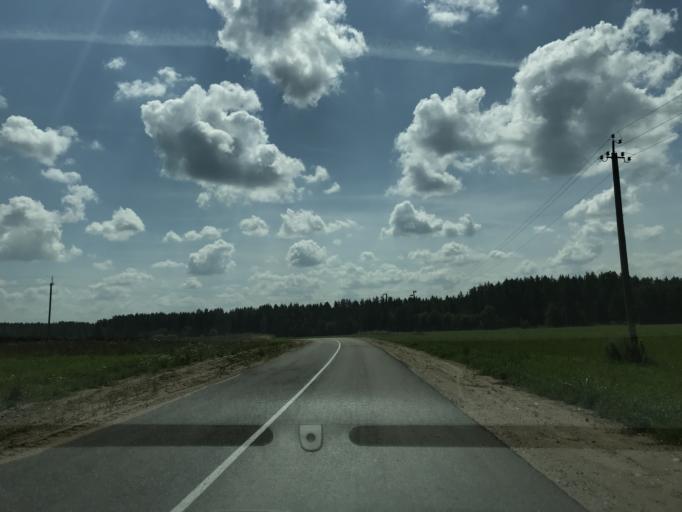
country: BY
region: Minsk
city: Rakaw
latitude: 54.0094
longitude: 26.9811
